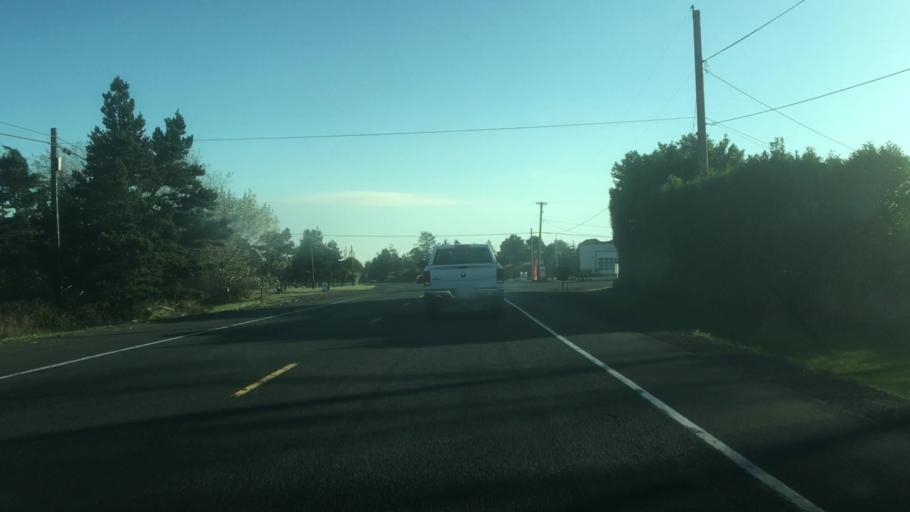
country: US
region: Oregon
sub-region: Clatsop County
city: Gearhart
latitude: 46.0772
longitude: -123.9168
